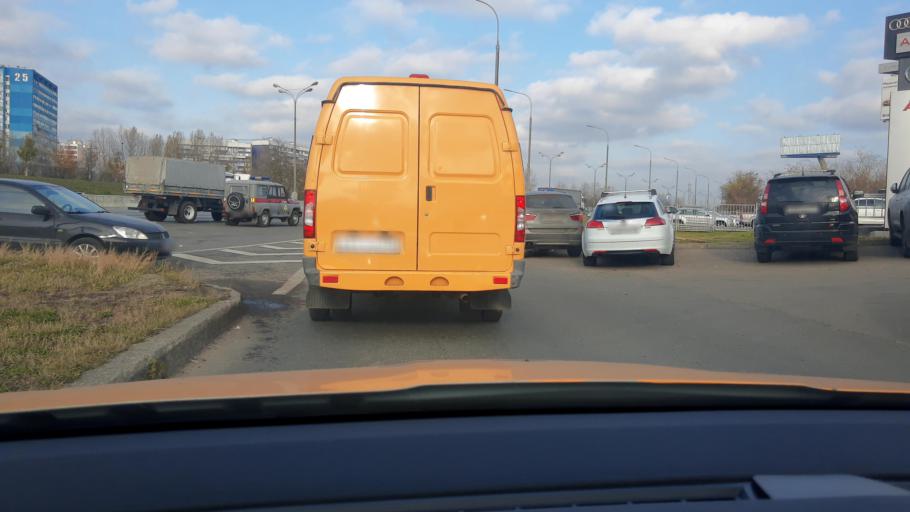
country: RU
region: Moskovskaya
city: Alekseyevka
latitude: 55.6272
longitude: 37.8004
